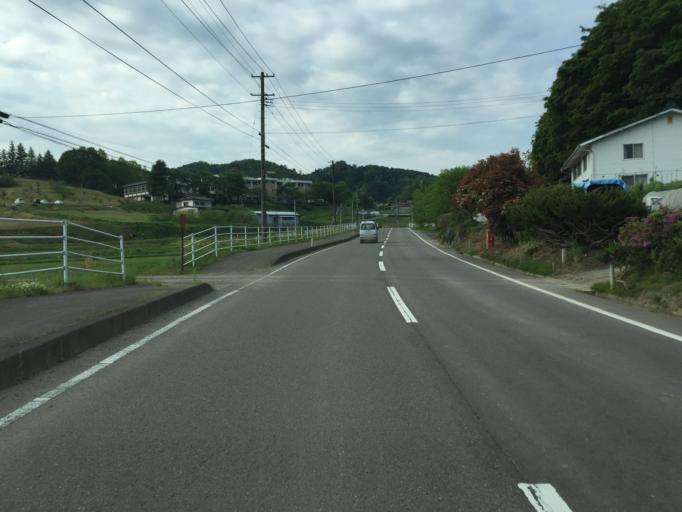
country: JP
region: Fukushima
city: Hobaramachi
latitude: 37.7213
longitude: 140.5943
